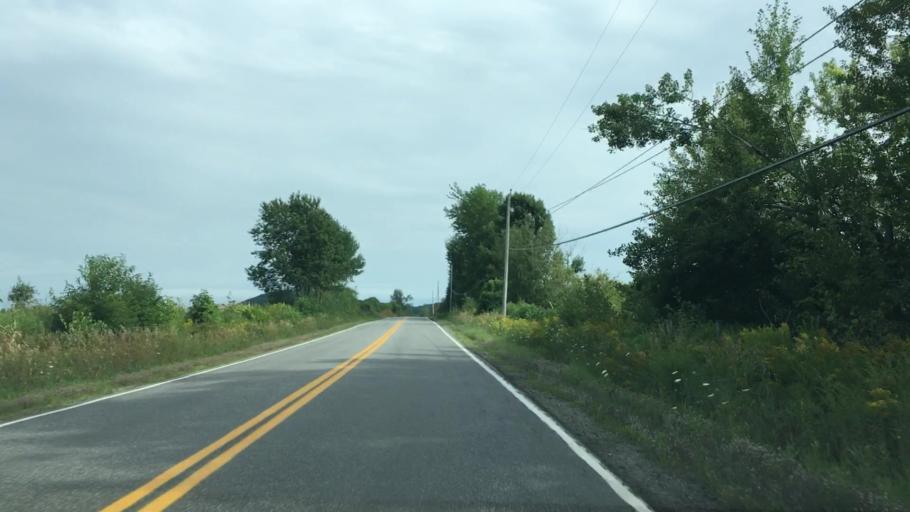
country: US
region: Maine
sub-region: Waldo County
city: Belfast
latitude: 44.3781
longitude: -69.0336
